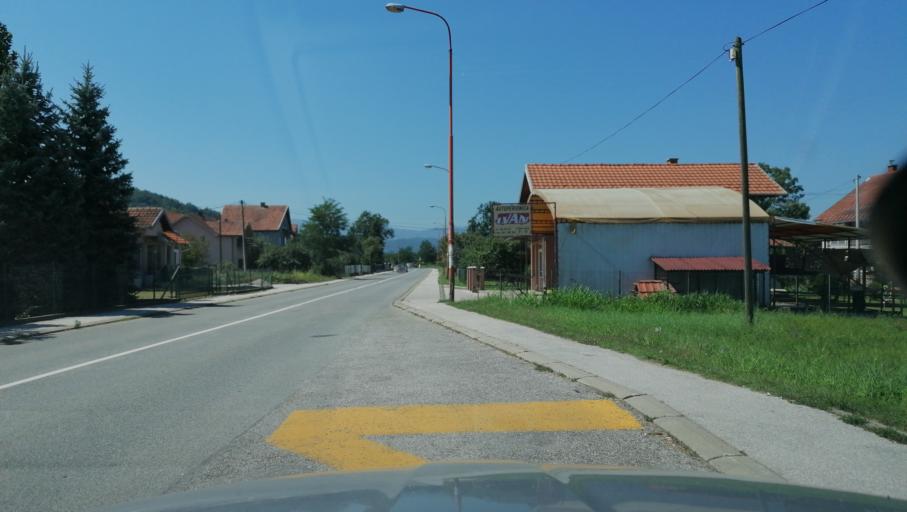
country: RS
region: Central Serbia
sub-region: Raski Okrug
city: Kraljevo
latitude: 43.6927
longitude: 20.6337
